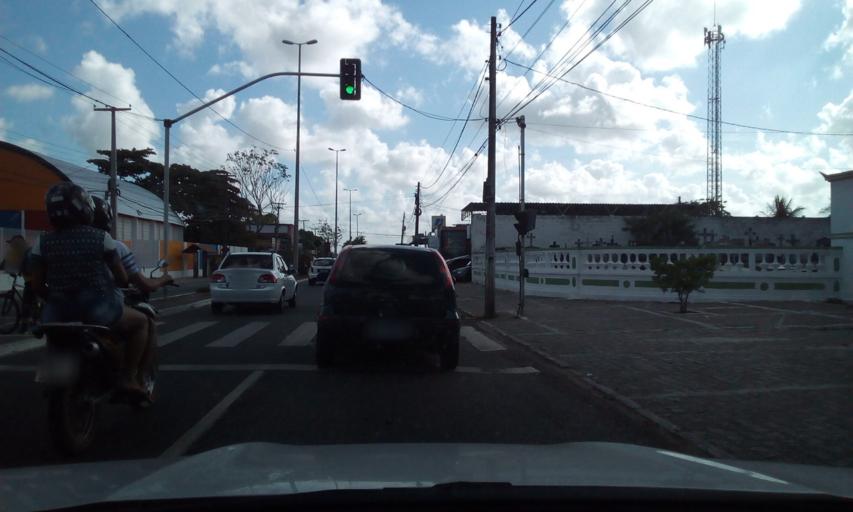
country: BR
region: Paraiba
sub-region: Bayeux
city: Bayeux
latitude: -7.1494
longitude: -34.8935
